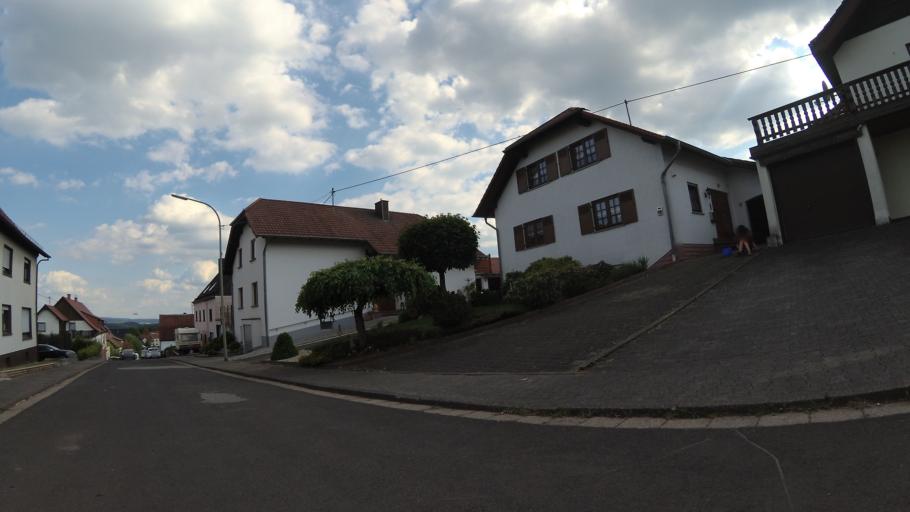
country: DE
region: Saarland
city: Oberthal
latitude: 49.5211
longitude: 7.0988
